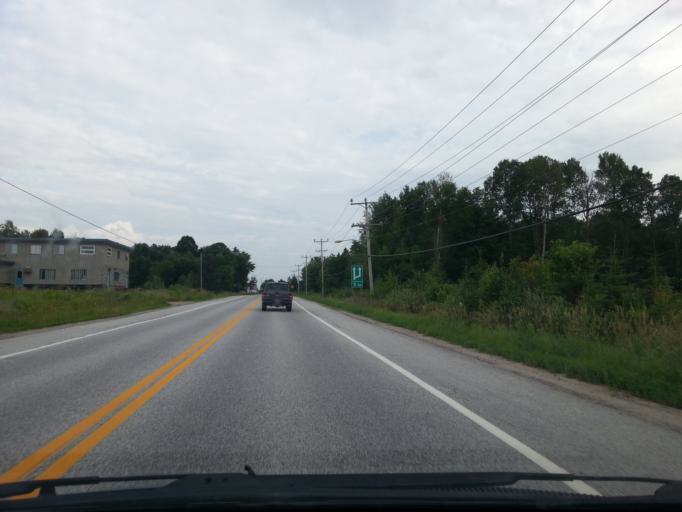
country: CA
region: Quebec
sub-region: Outaouais
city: Wakefield
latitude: 45.8719
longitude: -76.0236
